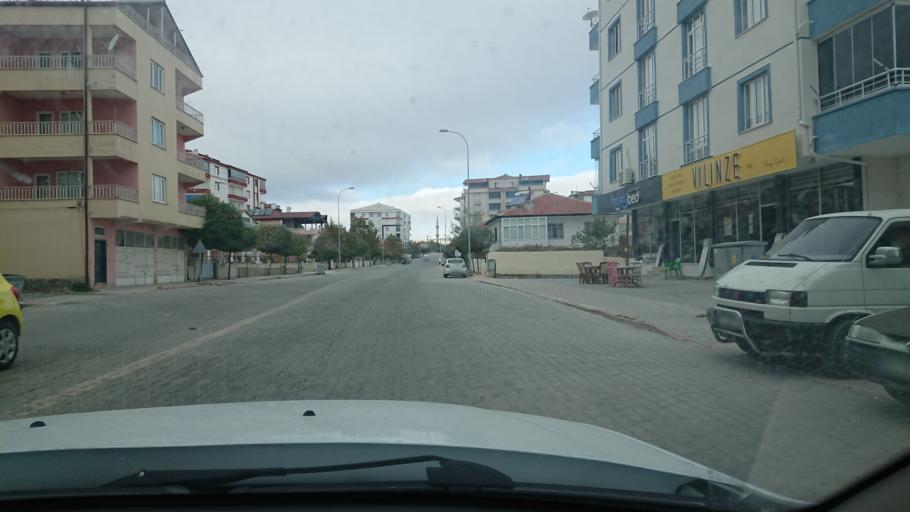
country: TR
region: Aksaray
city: Ortakoy
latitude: 38.7405
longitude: 34.0357
